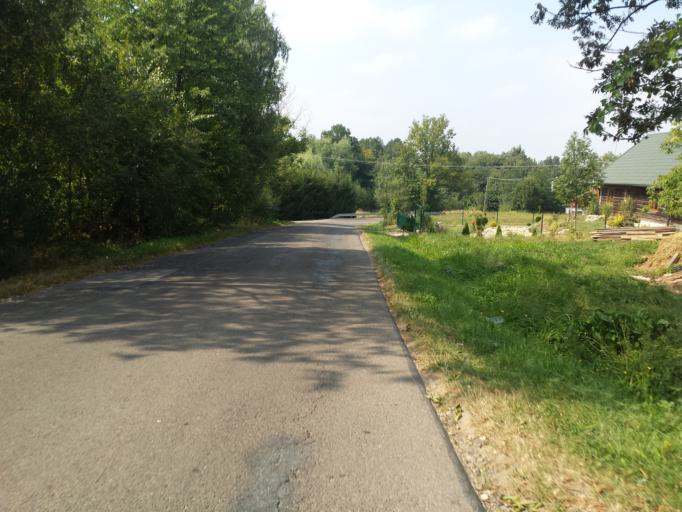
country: PL
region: Subcarpathian Voivodeship
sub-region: Powiat rzeszowski
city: Blazowa
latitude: 49.8456
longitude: 22.1418
